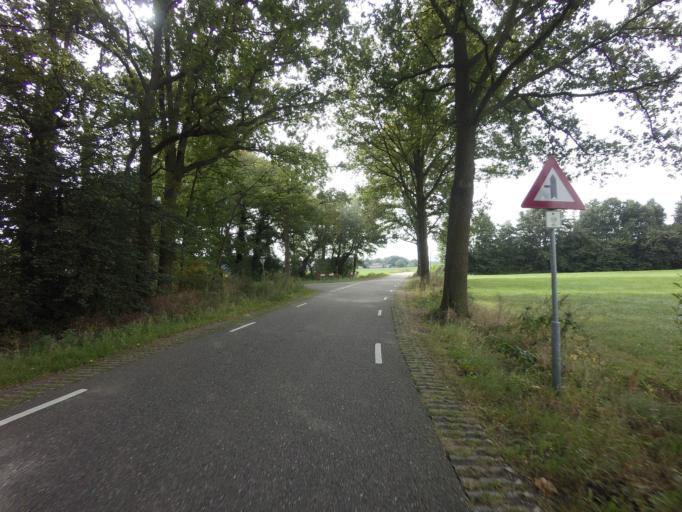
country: DE
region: Lower Saxony
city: Nordhorn
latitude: 52.3988
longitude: 7.0072
